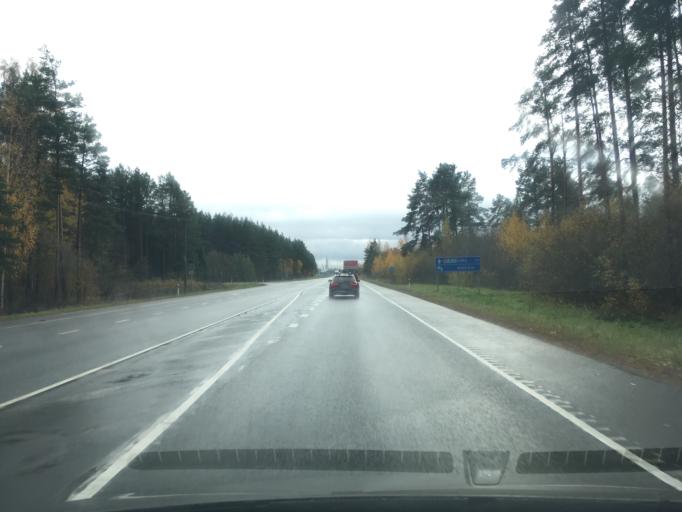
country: EE
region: Tartu
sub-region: Tartu linn
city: Tartu
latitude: 58.3884
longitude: 26.6677
